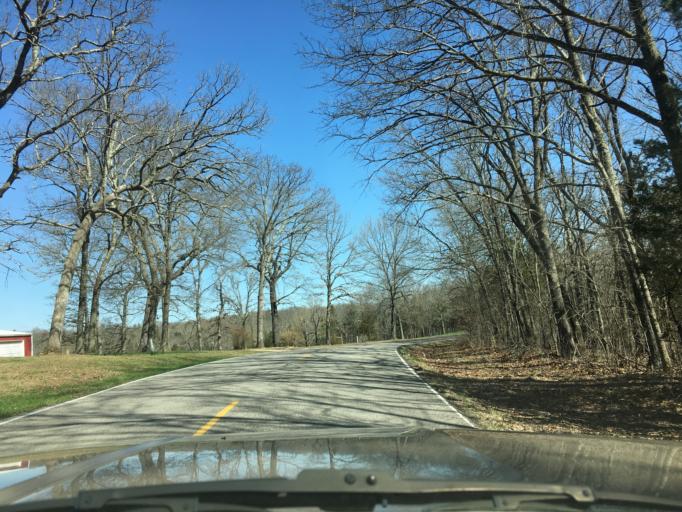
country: US
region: Missouri
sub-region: Franklin County
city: Gerald
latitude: 38.5330
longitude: -91.3328
